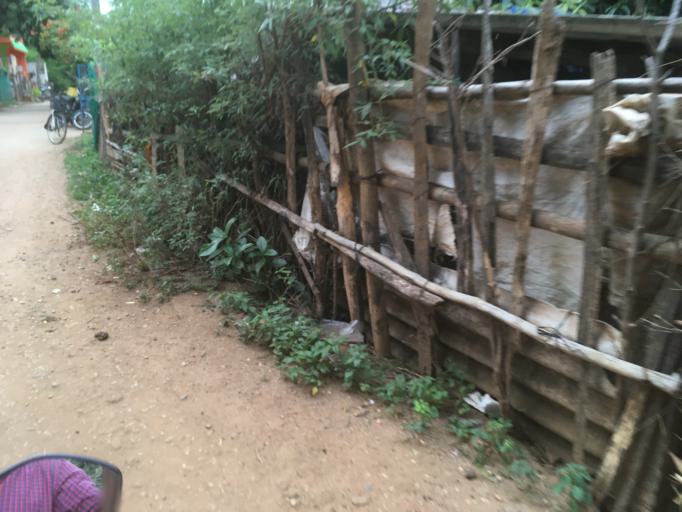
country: IN
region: Tamil Nadu
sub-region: Villupuram
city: Auroville
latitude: 12.0106
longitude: 79.8027
